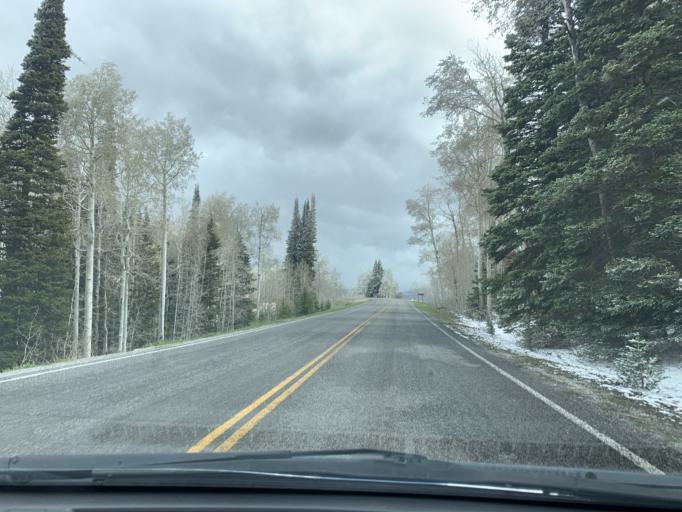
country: US
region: Utah
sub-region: Utah County
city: Elk Ridge
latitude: 39.8650
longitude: -111.6866
